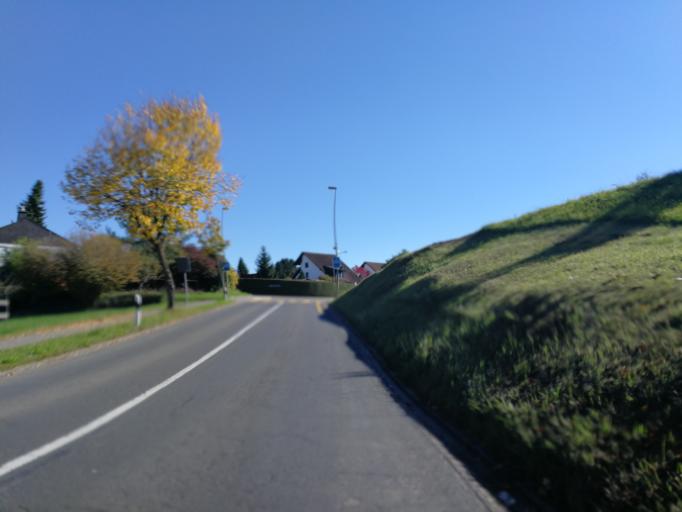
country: CH
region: Zurich
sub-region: Bezirk Meilen
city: Hombrechtikon
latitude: 47.2567
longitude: 8.7640
